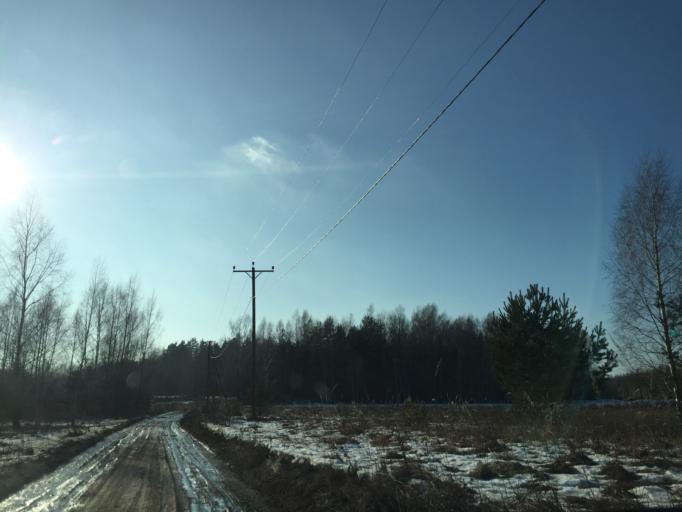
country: LV
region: Lecava
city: Iecava
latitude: 56.6799
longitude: 24.2017
